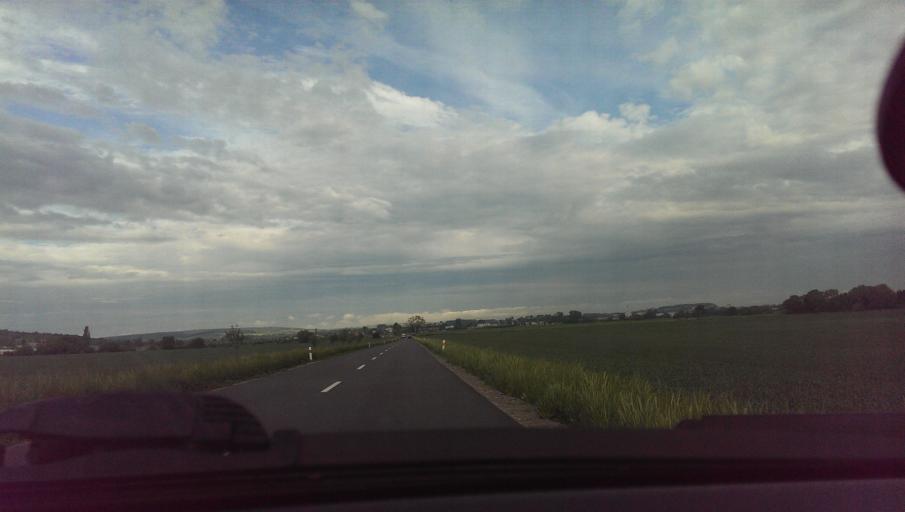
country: CZ
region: Zlin
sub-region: Okres Kromeriz
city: Kromeriz
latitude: 49.2715
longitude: 17.4250
